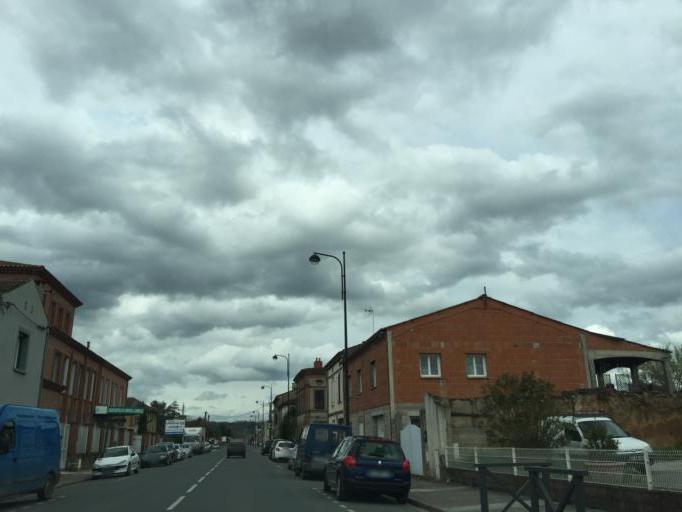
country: FR
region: Midi-Pyrenees
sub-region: Departement du Tarn
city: Albi
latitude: 43.9443
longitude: 2.1506
